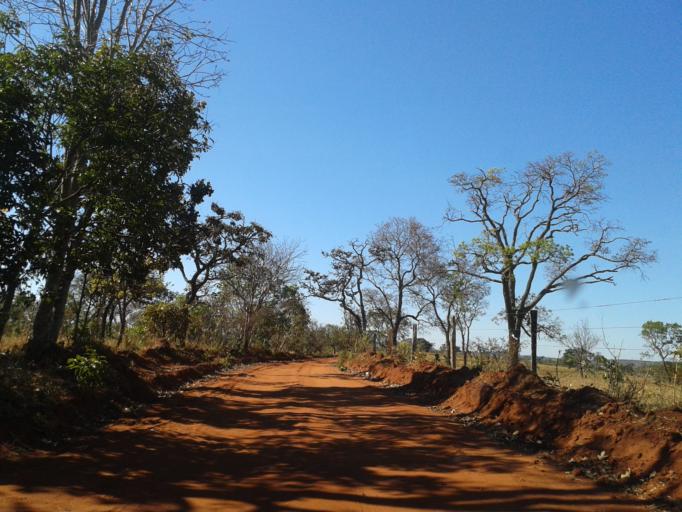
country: BR
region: Minas Gerais
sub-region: Ituiutaba
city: Ituiutaba
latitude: -19.0811
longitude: -49.3374
